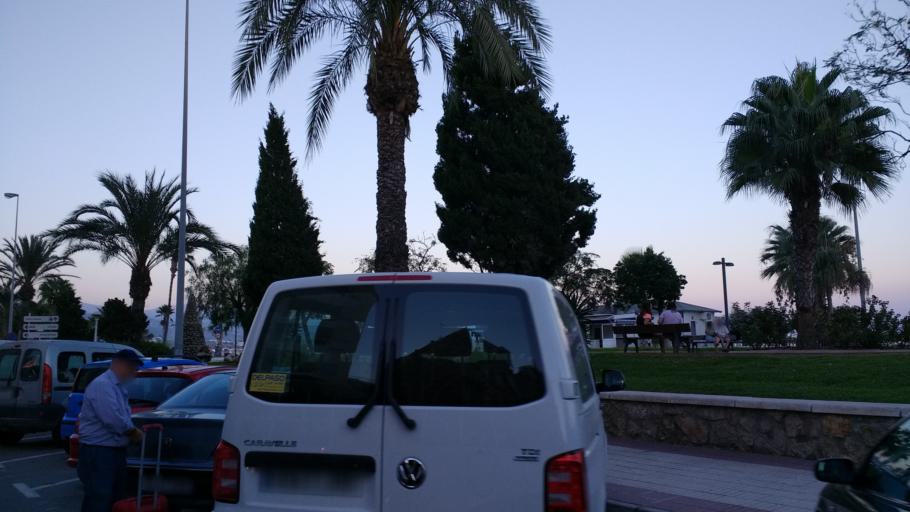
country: ES
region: Andalusia
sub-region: Provincia de Malaga
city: Velez-Malaga
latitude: 36.7426
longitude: -4.0887
